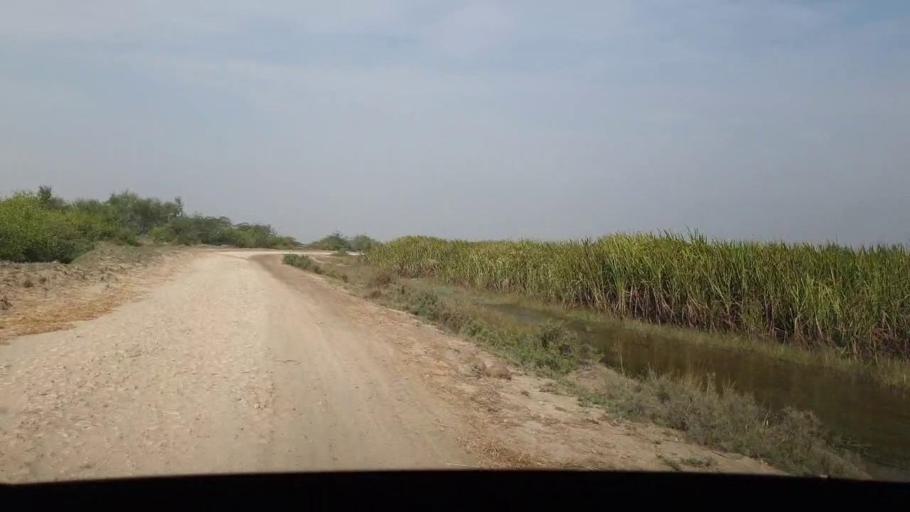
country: PK
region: Sindh
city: Chuhar Jamali
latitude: 24.3206
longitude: 67.9477
